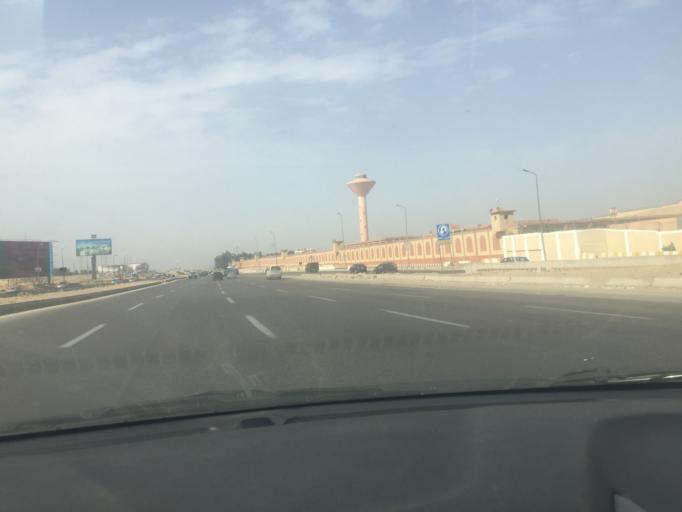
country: EG
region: Muhafazat al Qalyubiyah
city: Al Khankah
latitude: 30.0830
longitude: 31.4678
